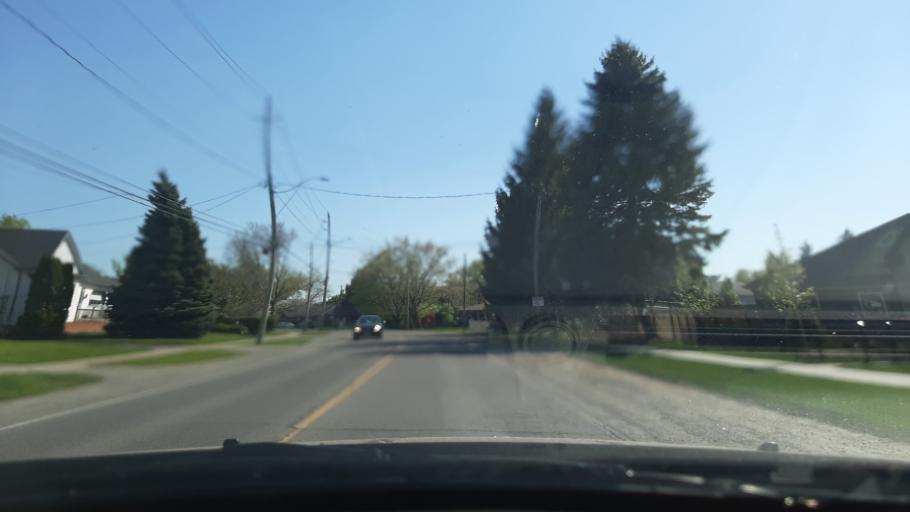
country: CA
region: Ontario
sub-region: Regional Municipality of Niagara
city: St. Catharines
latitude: 43.1958
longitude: -79.2256
